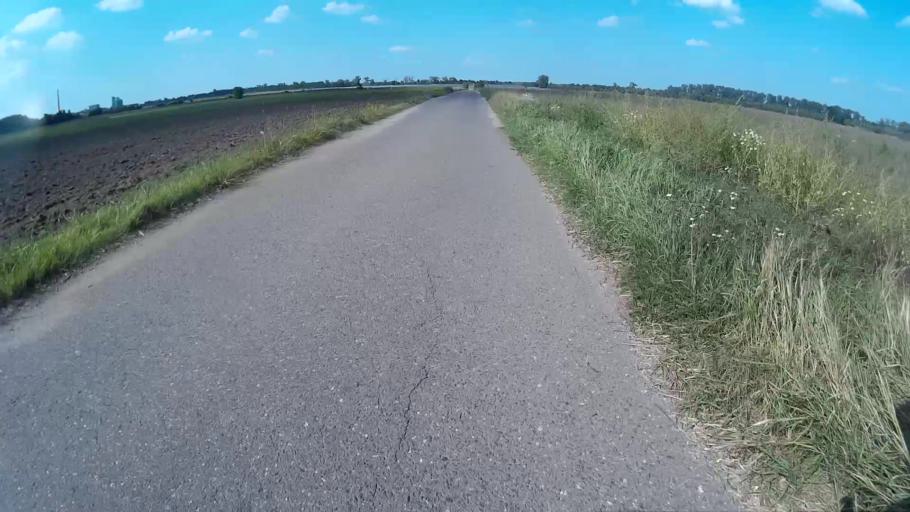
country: CZ
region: South Moravian
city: Hrusovany nad Jevisovkou
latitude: 48.8054
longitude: 16.4266
